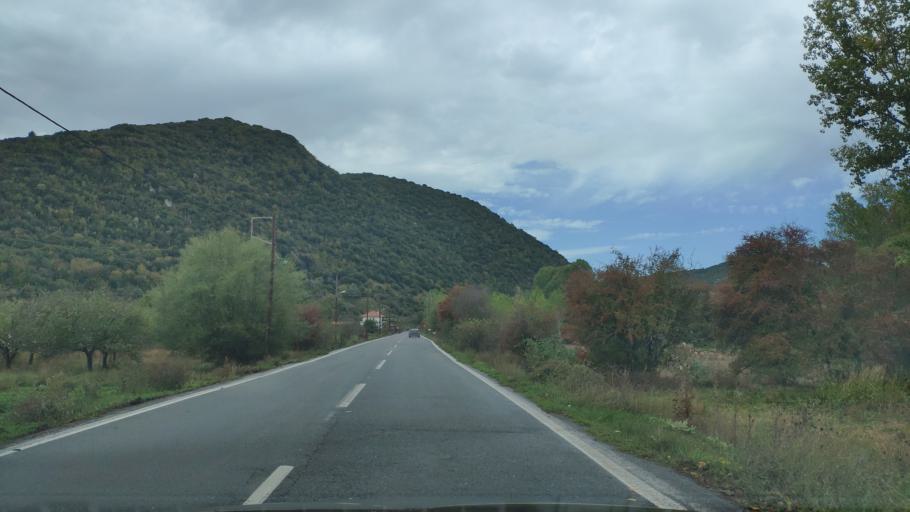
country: GR
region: Peloponnese
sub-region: Nomos Arkadias
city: Dimitsana
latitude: 37.6297
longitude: 22.0757
